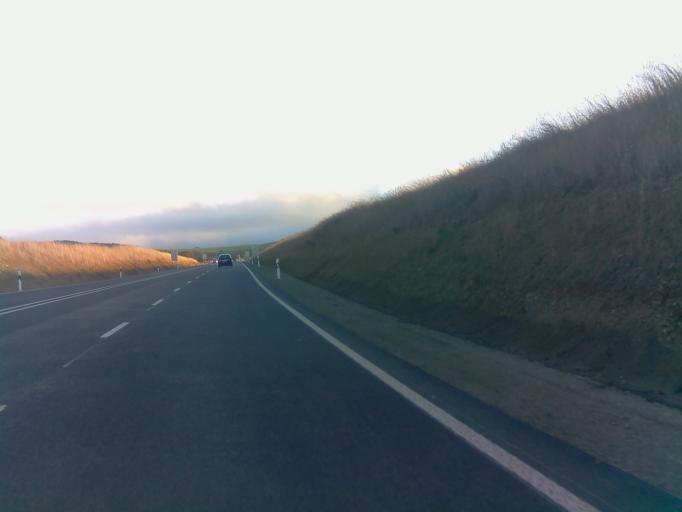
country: DE
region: Thuringia
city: Stadtilm
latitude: 50.7546
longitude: 11.0653
